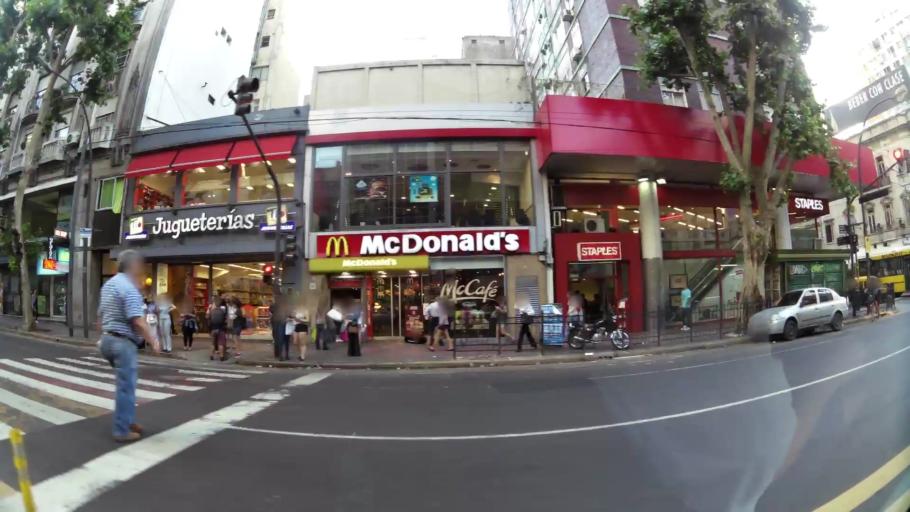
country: AR
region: Buenos Aires F.D.
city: Retiro
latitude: -34.5946
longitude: -58.4021
